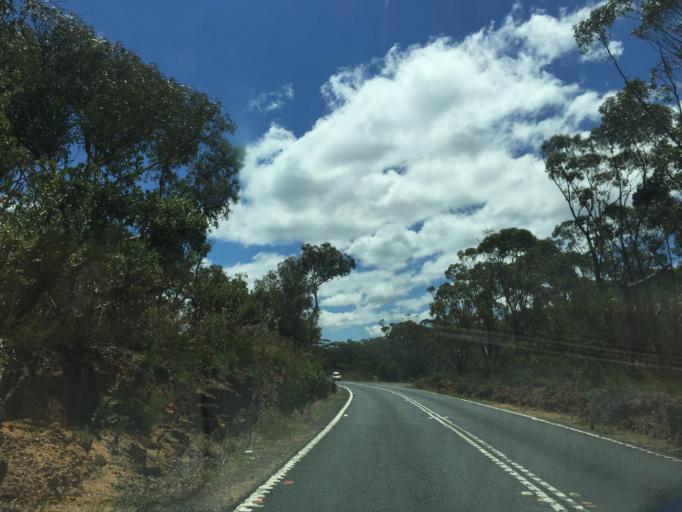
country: AU
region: New South Wales
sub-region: Blue Mountains Municipality
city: Blackheath
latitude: -33.5692
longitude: 150.3502
